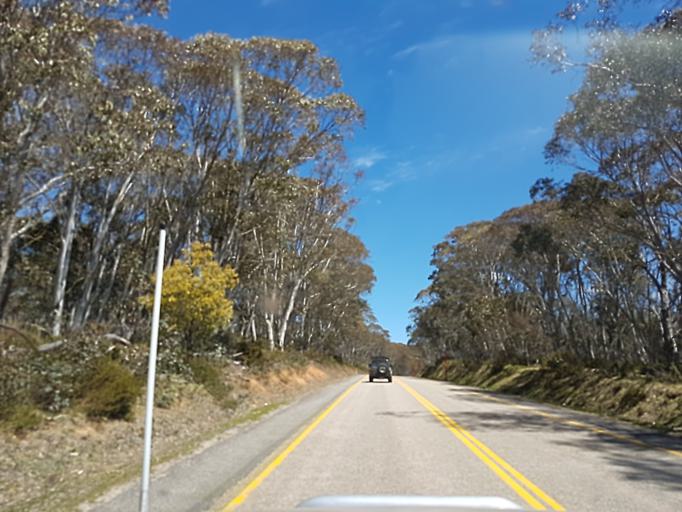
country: AU
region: Victoria
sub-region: Alpine
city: Mount Beauty
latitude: -37.0257
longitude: 147.2746
